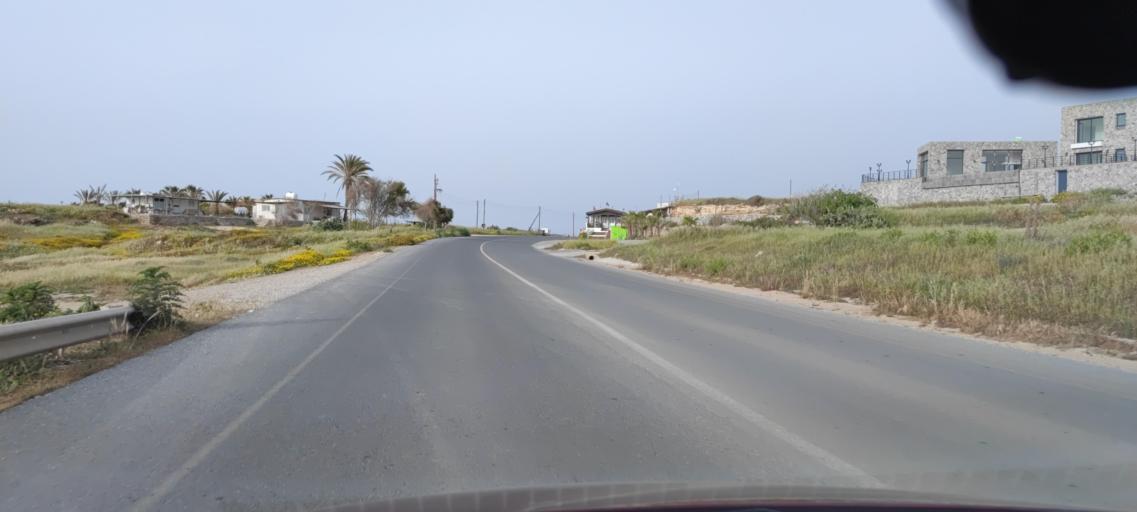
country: CY
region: Ammochostos
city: Rizokarpaso
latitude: 35.5679
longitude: 34.2504
